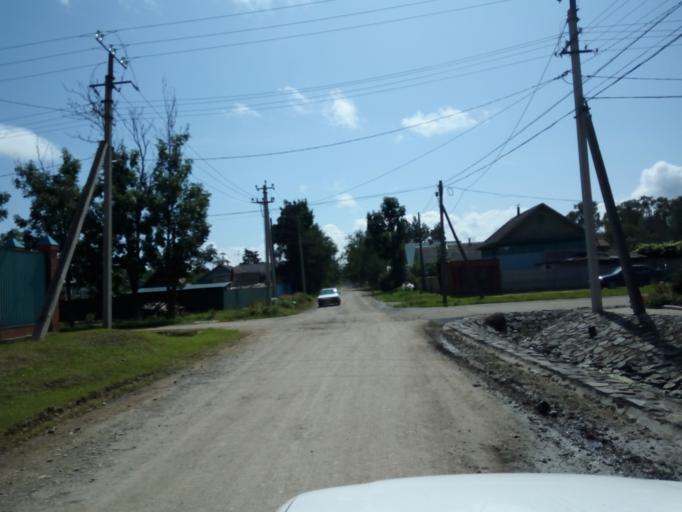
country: RU
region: Primorskiy
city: Dal'nerechensk
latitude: 45.9322
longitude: 133.7382
